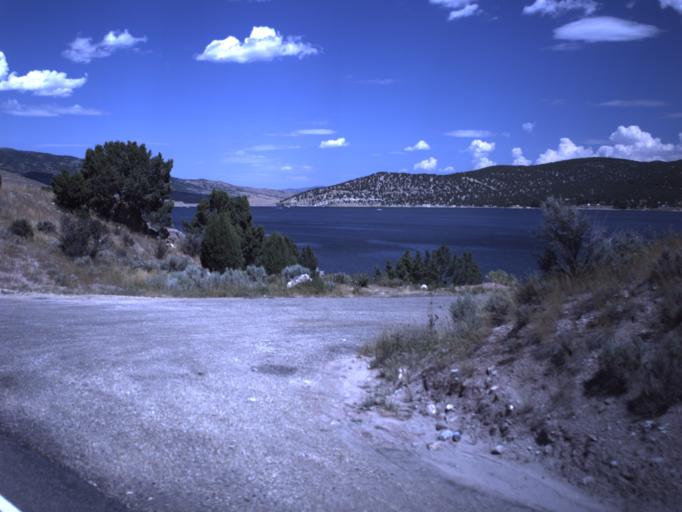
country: US
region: Utah
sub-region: Summit County
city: Oakley
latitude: 40.7666
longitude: -111.3997
